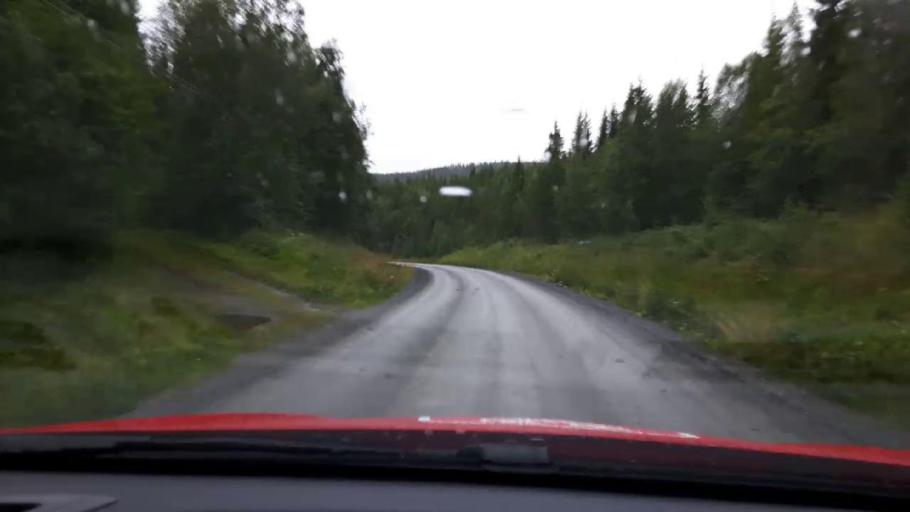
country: SE
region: Jaemtland
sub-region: Are Kommun
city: Are
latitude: 63.4765
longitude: 12.8093
